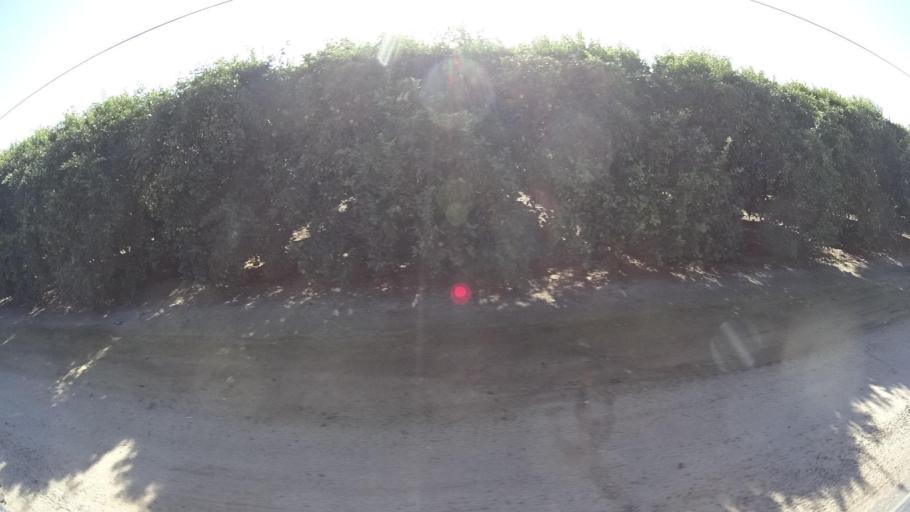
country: US
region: California
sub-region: Tulare County
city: Richgrove
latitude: 35.7180
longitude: -119.1371
